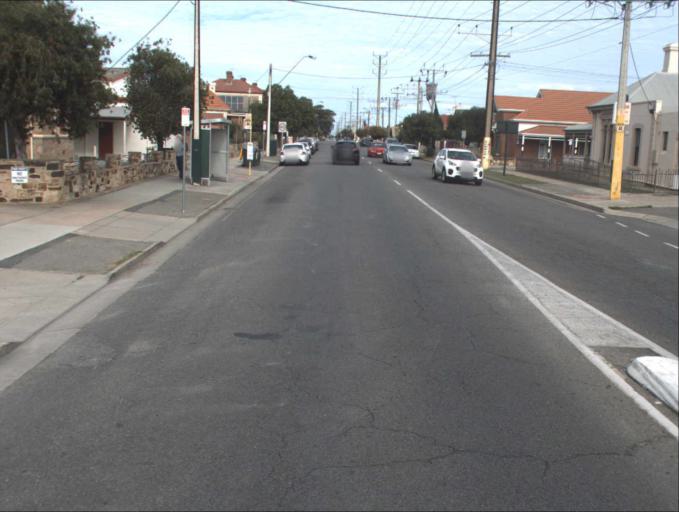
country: AU
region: South Australia
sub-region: Port Adelaide Enfield
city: Birkenhead
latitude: -34.8393
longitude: 138.4838
